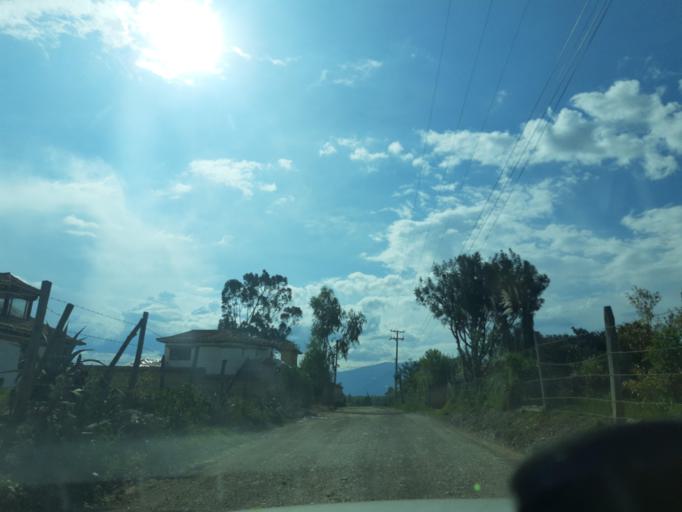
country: CO
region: Boyaca
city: Villa de Leiva
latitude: 5.6609
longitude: -73.5399
